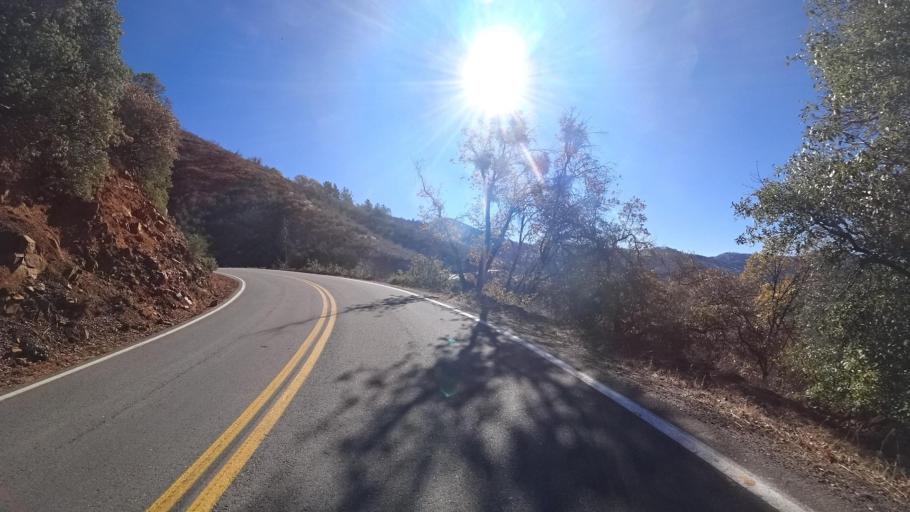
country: US
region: California
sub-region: Kern County
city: Alta Sierra
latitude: 35.7463
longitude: -118.5826
